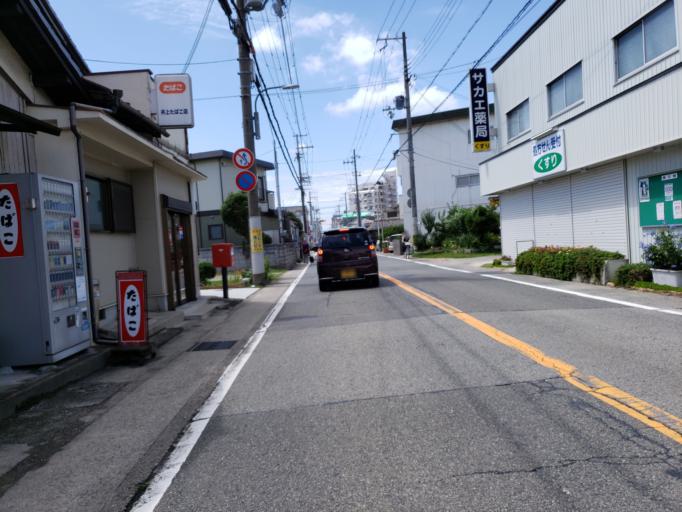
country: JP
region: Hyogo
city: Kakogawacho-honmachi
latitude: 34.7065
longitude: 134.8904
